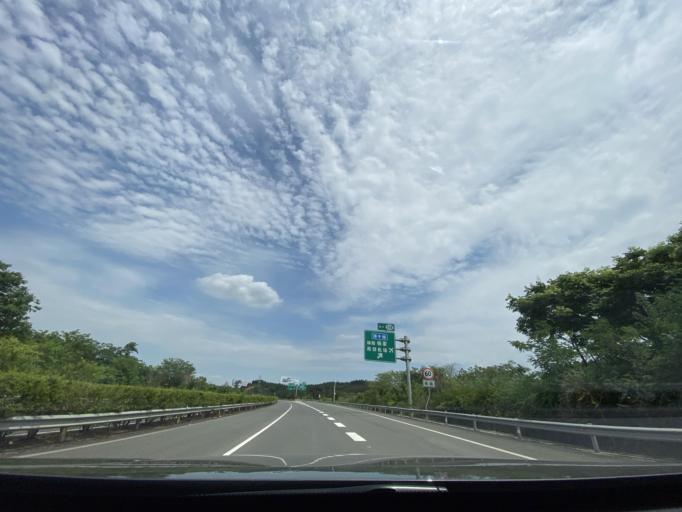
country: CN
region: Sichuan
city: Mianyang
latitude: 31.3520
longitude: 104.7035
